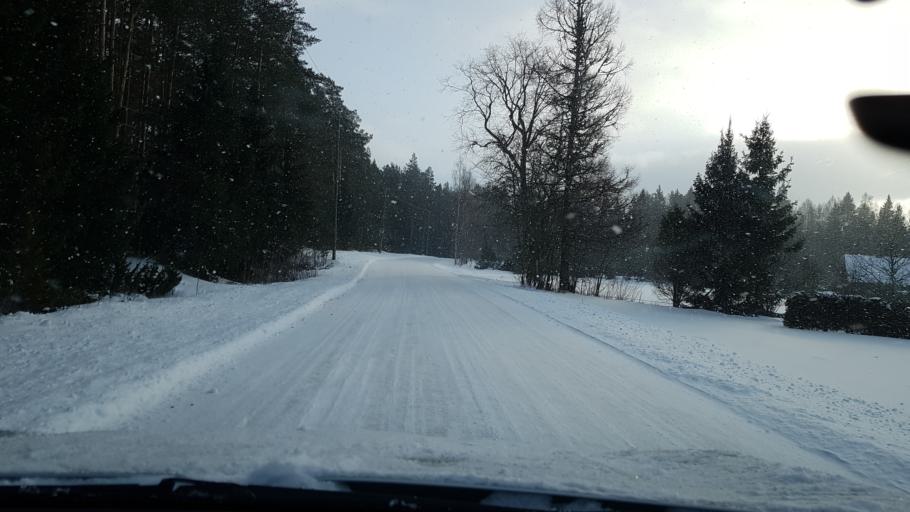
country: EE
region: Harju
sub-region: Nissi vald
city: Turba
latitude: 59.1875
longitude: 24.1395
